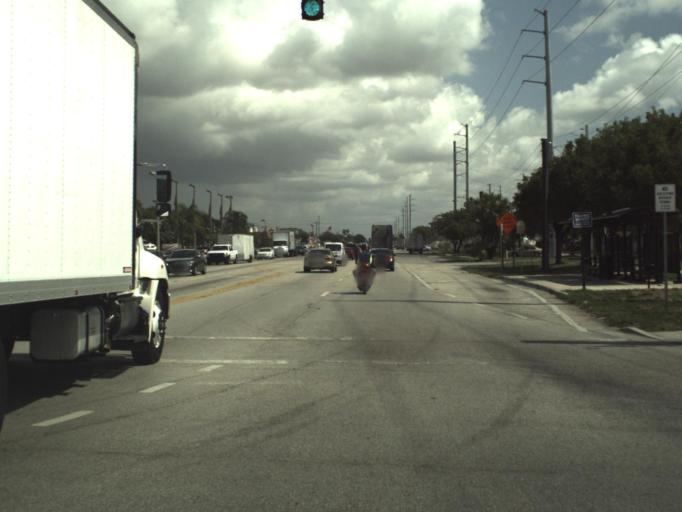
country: US
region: Florida
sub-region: Broward County
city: West Park
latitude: 25.9953
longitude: -80.2070
